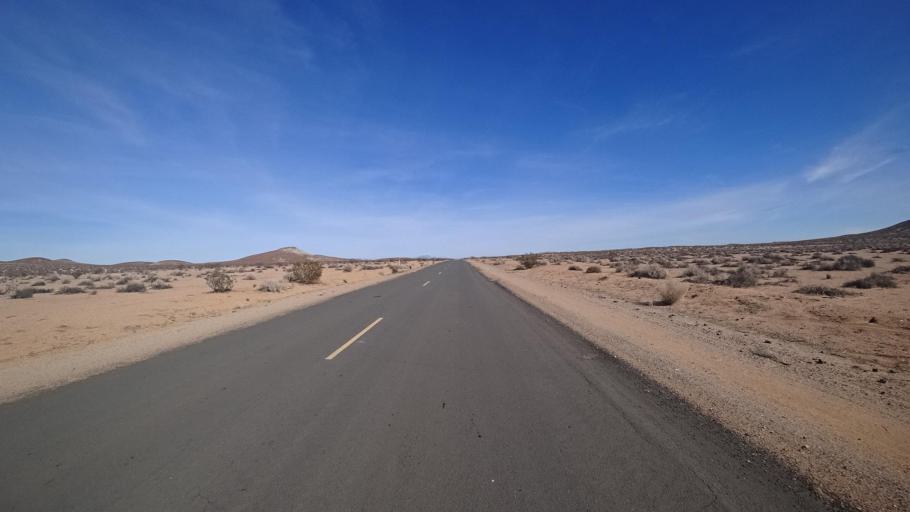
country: US
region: California
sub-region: Kern County
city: North Edwards
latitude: 35.0460
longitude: -117.8206
